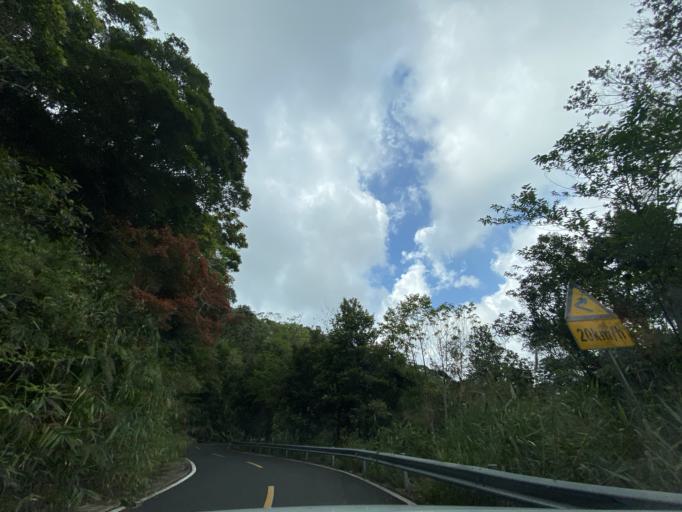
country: CN
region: Hainan
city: Diaoluoshan
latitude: 18.7170
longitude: 109.8795
